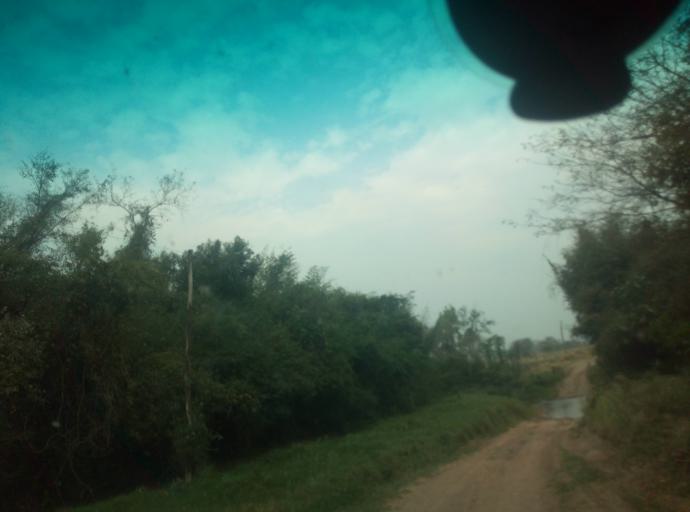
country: PY
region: Caaguazu
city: San Joaquin
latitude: -25.1050
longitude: -56.1279
